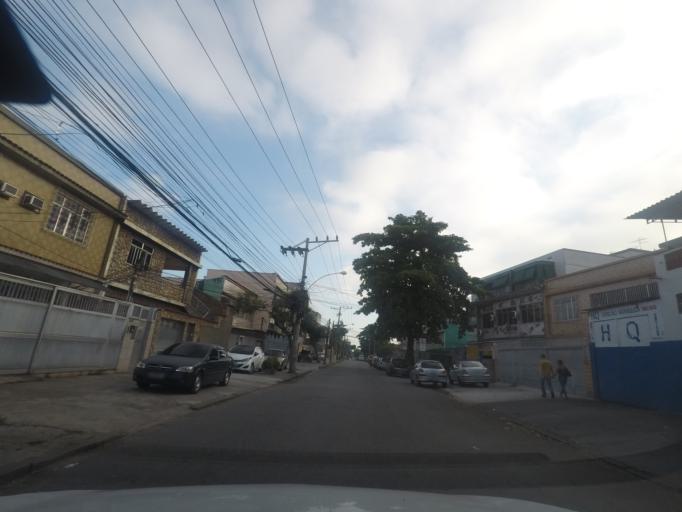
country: BR
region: Rio de Janeiro
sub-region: Duque De Caxias
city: Duque de Caxias
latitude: -22.8358
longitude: -43.2798
